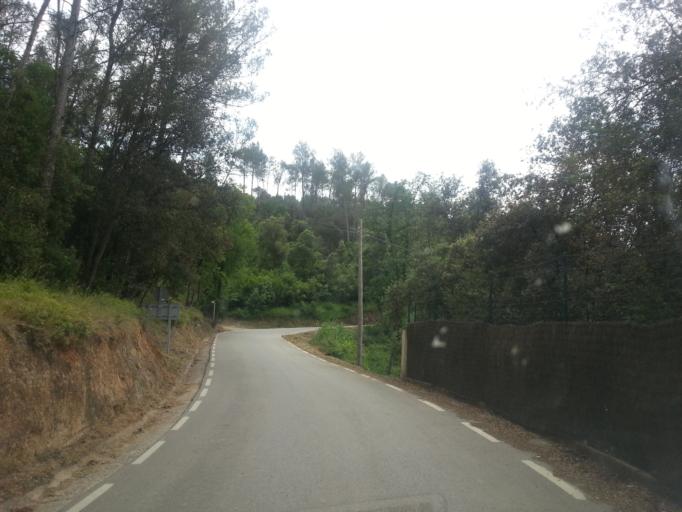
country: ES
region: Catalonia
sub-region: Provincia de Barcelona
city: Molins de Rei
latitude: 41.4345
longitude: 2.0432
